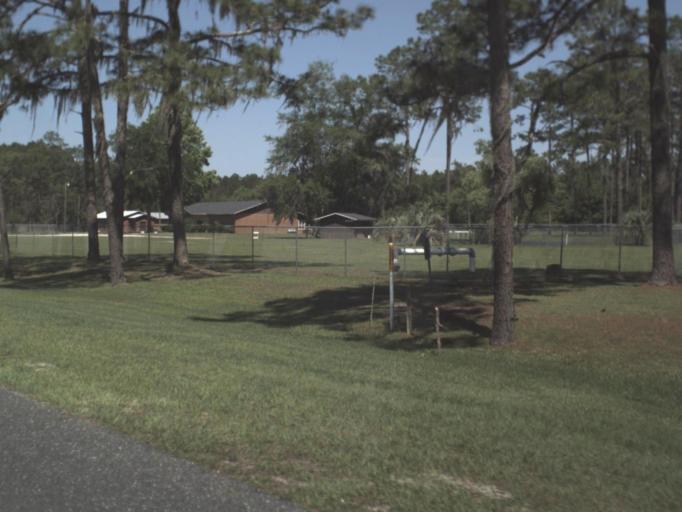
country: US
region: Florida
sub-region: Union County
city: Lake Butler
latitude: 30.2184
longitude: -82.3644
